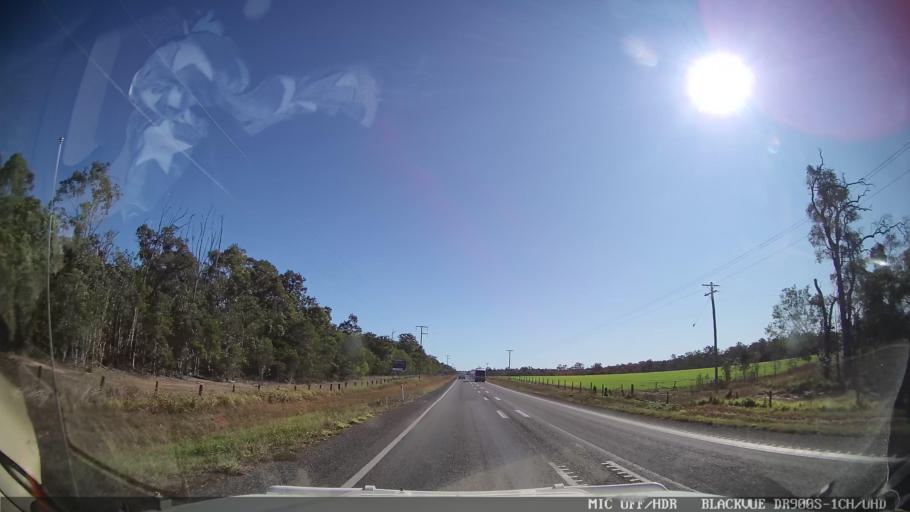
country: AU
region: Queensland
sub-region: Bundaberg
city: Childers
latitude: -25.2510
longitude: 152.3531
